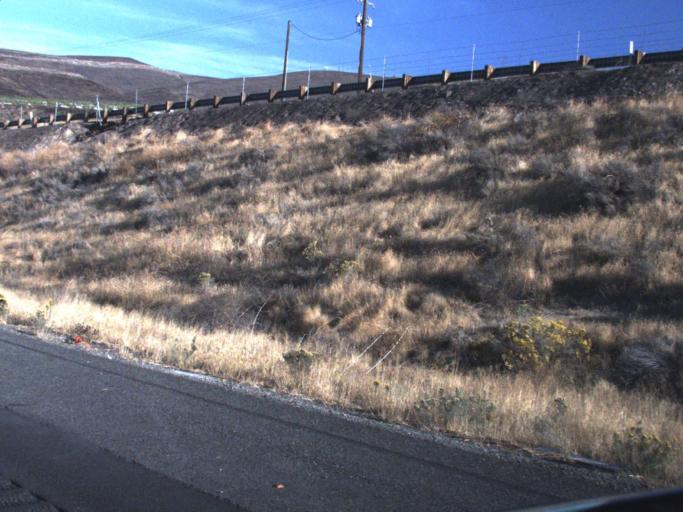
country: US
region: Washington
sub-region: Yakima County
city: Union Gap
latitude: 46.5185
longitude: -120.4571
